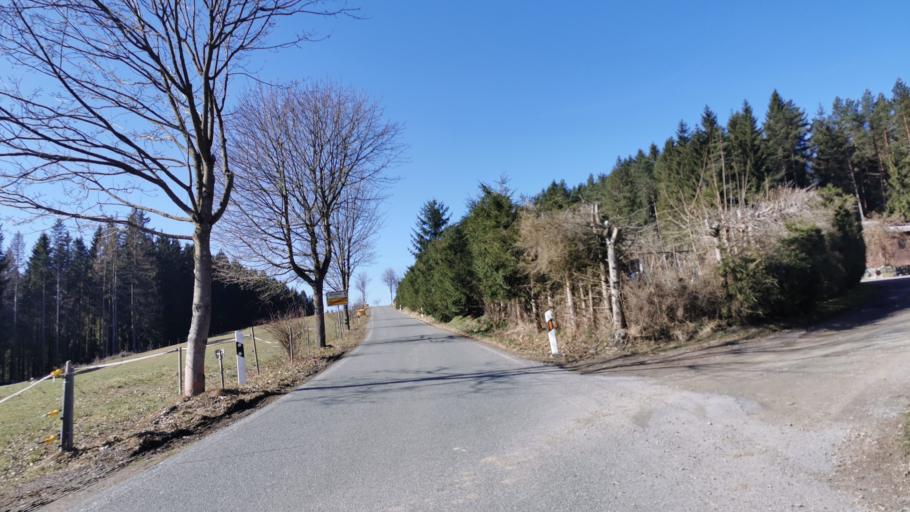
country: DE
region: Thuringia
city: Wurzbach
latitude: 50.4538
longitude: 11.5252
